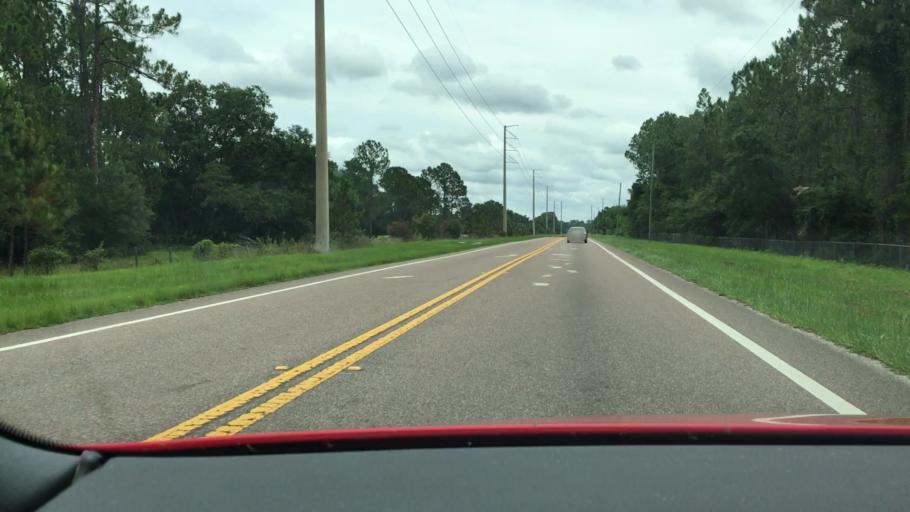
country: US
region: Florida
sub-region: Lake County
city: Eustis
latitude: 28.8753
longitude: -81.6804
